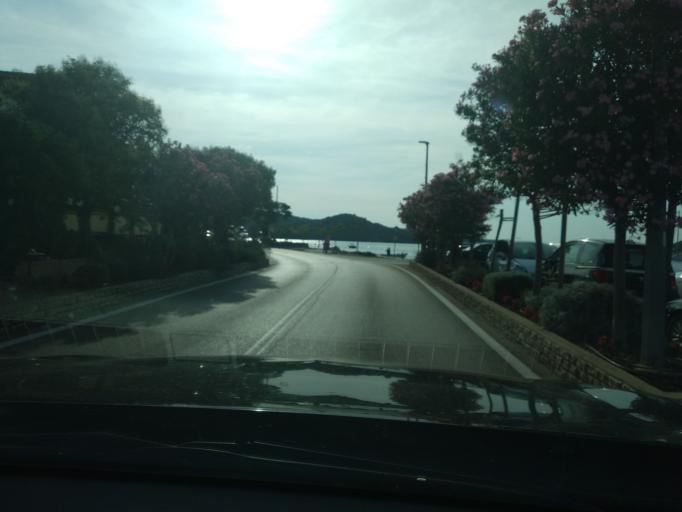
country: HR
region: Sibensko-Kniniska
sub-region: Grad Sibenik
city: Tisno
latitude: 43.7992
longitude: 15.6402
